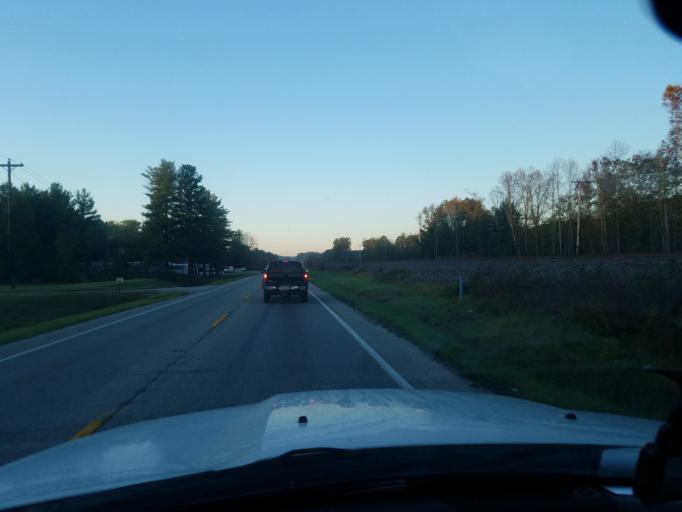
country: US
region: Kentucky
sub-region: Laurel County
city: North Corbin
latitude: 37.0400
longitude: -84.0567
